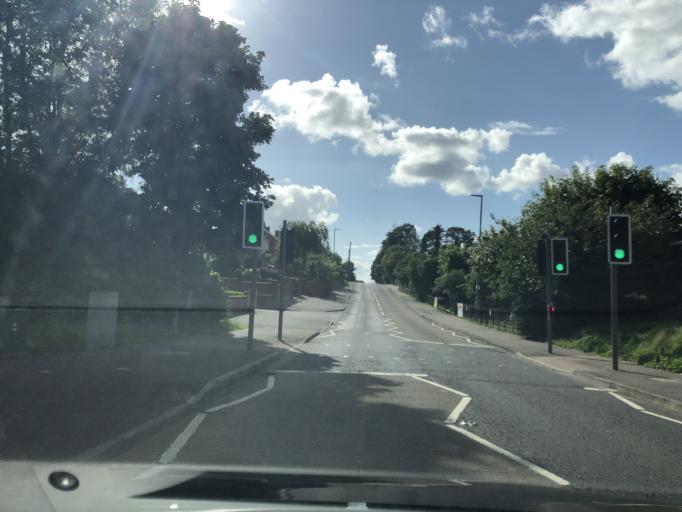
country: GB
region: Northern Ireland
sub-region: Castlereagh District
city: Dundonald
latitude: 54.5867
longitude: -5.8080
